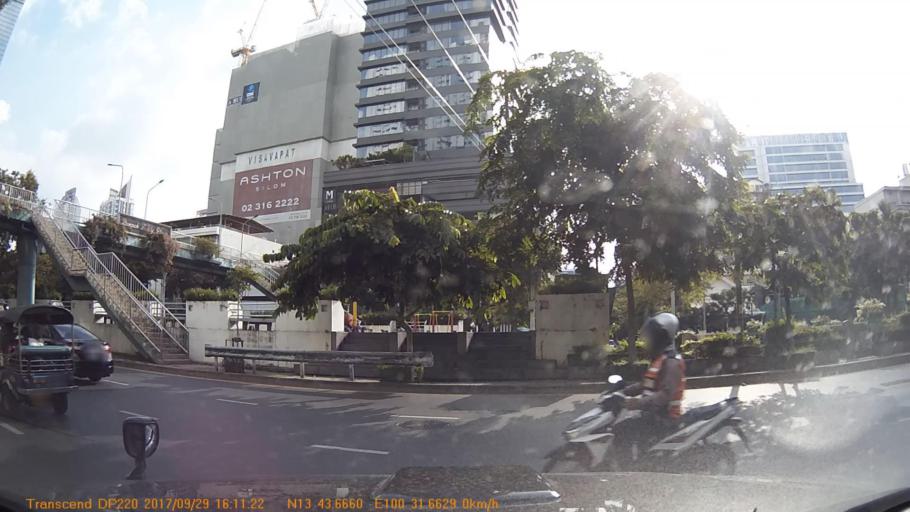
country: TH
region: Bangkok
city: Bang Rak
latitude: 13.7276
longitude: 100.5277
